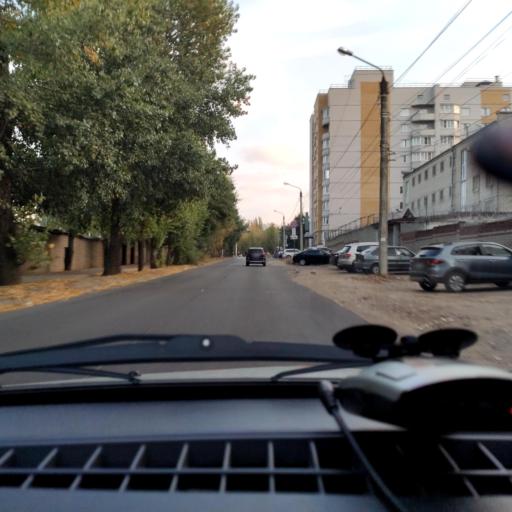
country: RU
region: Voronezj
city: Voronezh
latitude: 51.6573
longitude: 39.1377
